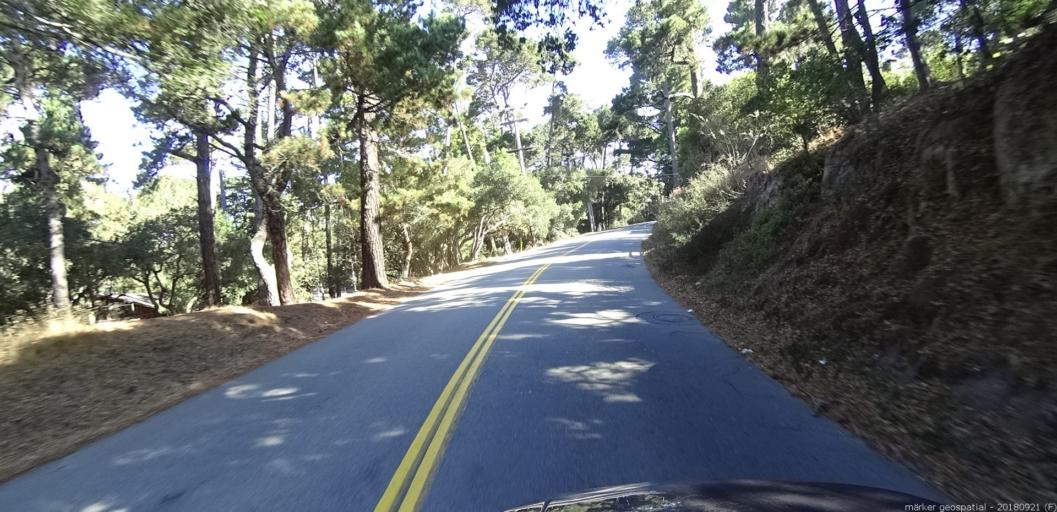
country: US
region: California
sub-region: Monterey County
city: Carmel-by-the-Sea
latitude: 36.5617
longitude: -121.9200
